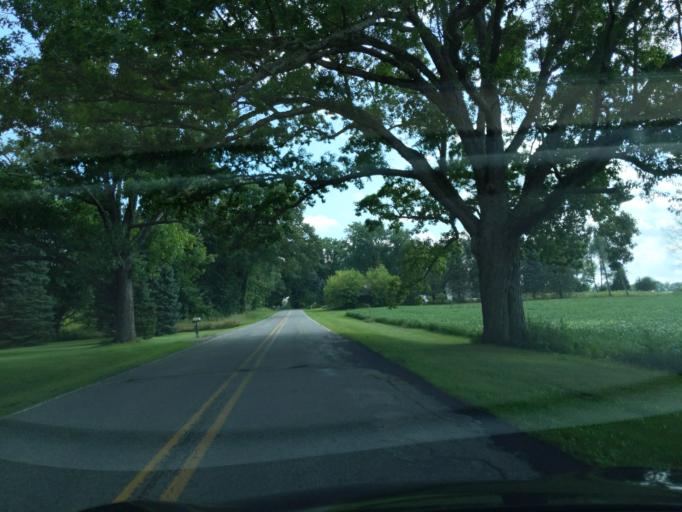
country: US
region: Michigan
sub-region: Jackson County
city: Spring Arbor
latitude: 42.3128
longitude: -84.5193
